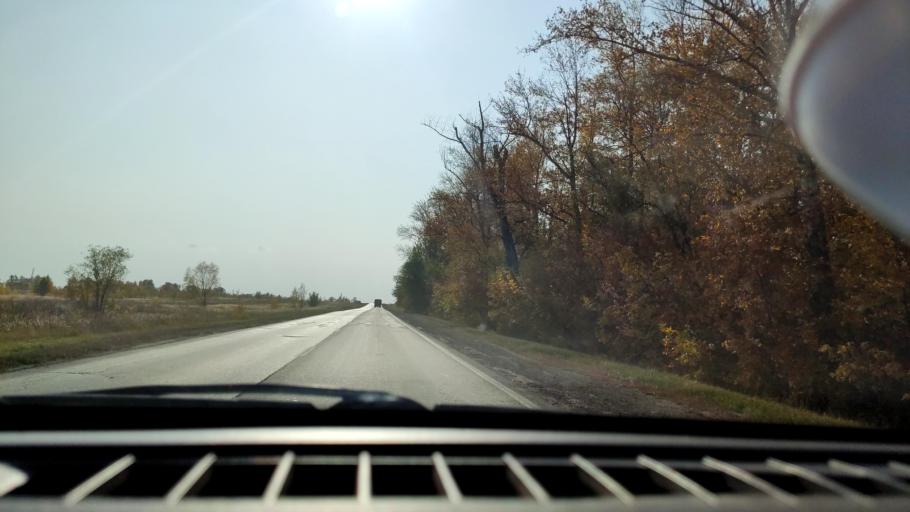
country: RU
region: Samara
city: Smyshlyayevka
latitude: 53.1196
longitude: 50.3655
